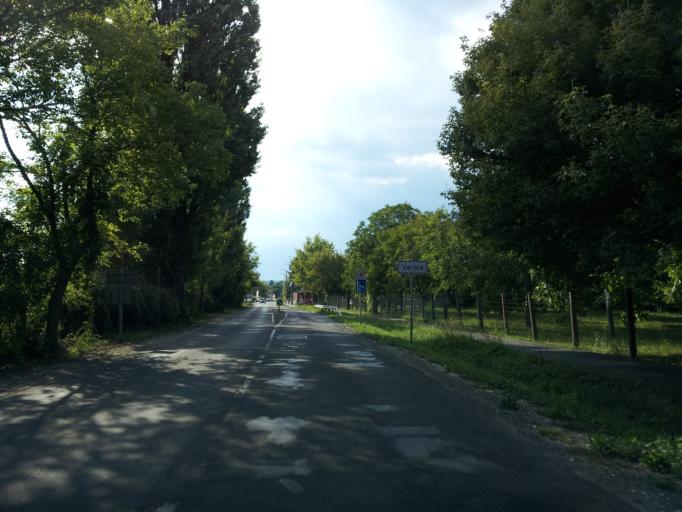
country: HU
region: Pest
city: Veroce
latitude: 47.8202
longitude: 19.0445
